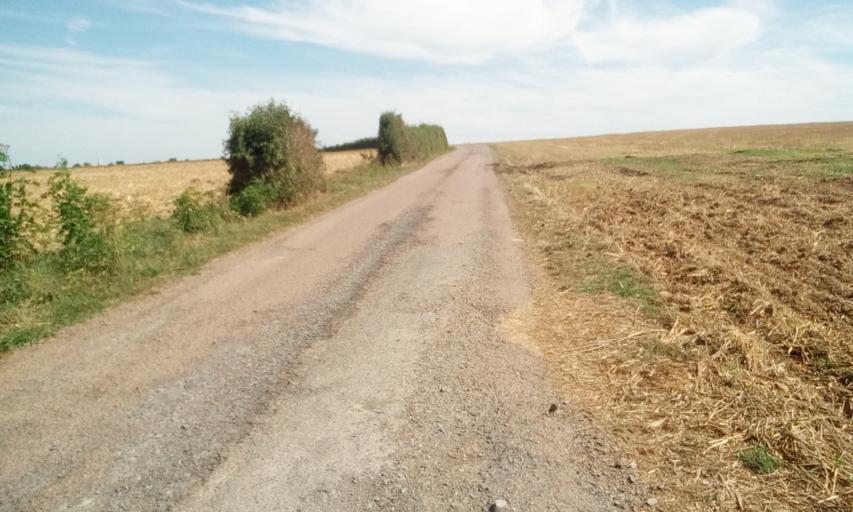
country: FR
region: Lower Normandy
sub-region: Departement du Calvados
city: Bretteville-sur-Odon
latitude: 49.1537
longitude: -0.4113
